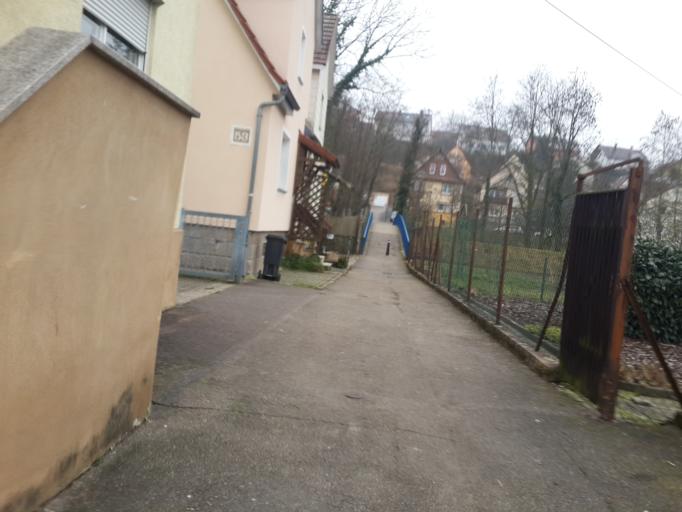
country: DE
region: Baden-Wuerttemberg
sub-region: Regierungsbezirk Stuttgart
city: Neckarsulm
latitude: 49.1667
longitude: 9.2013
